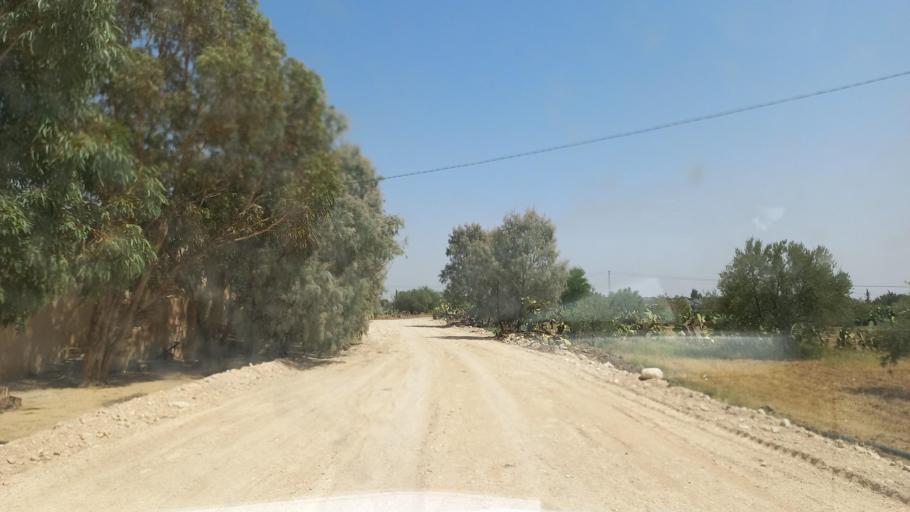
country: TN
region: Al Qasrayn
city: Kasserine
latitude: 35.2467
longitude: 9.0277
